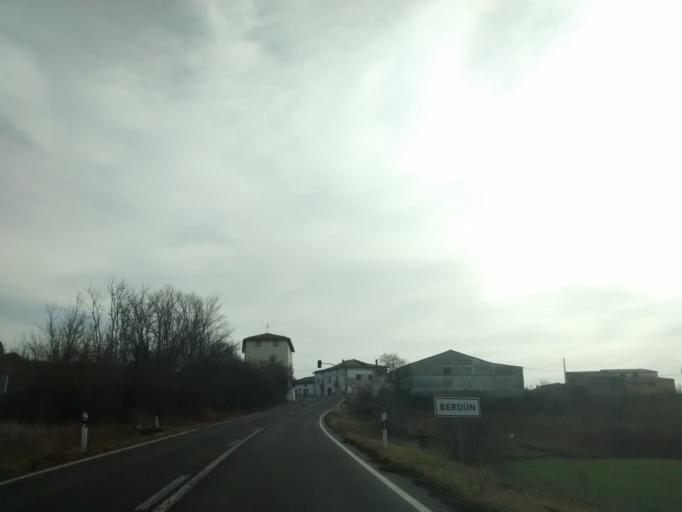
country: ES
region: Aragon
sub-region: Provincia de Zaragoza
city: Mianos
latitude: 42.6003
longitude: -0.8608
